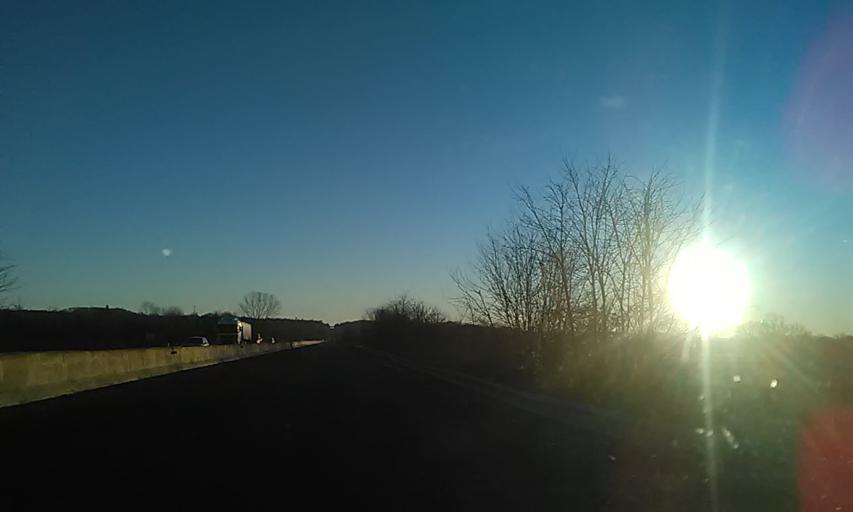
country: IT
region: Piedmont
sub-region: Provincia di Biella
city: Cossato
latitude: 45.5529
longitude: 8.1843
